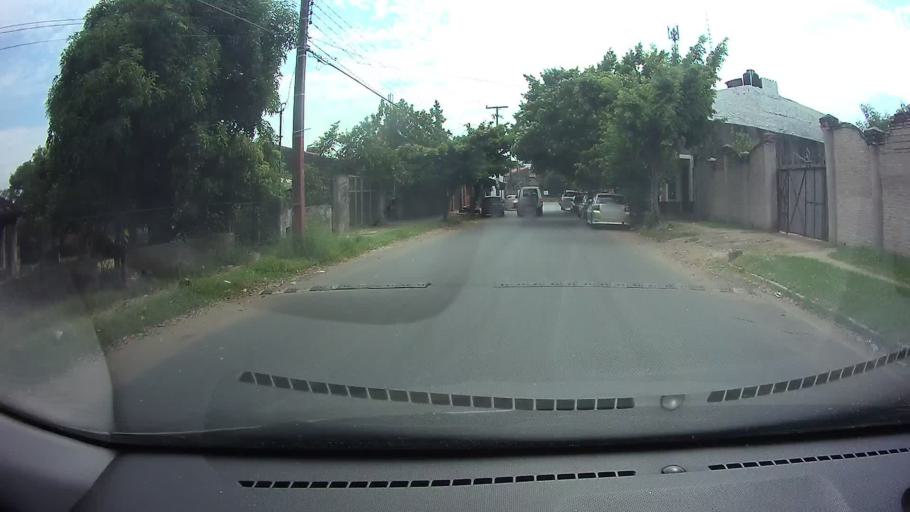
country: PY
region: Central
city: Fernando de la Mora
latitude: -25.3025
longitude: -57.5410
